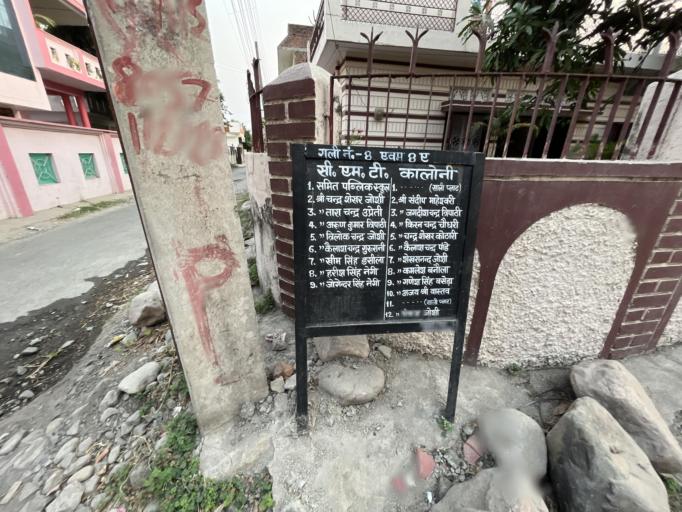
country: IN
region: Uttarakhand
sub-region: Naini Tal
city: Haldwani
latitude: 29.1994
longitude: 79.5110
